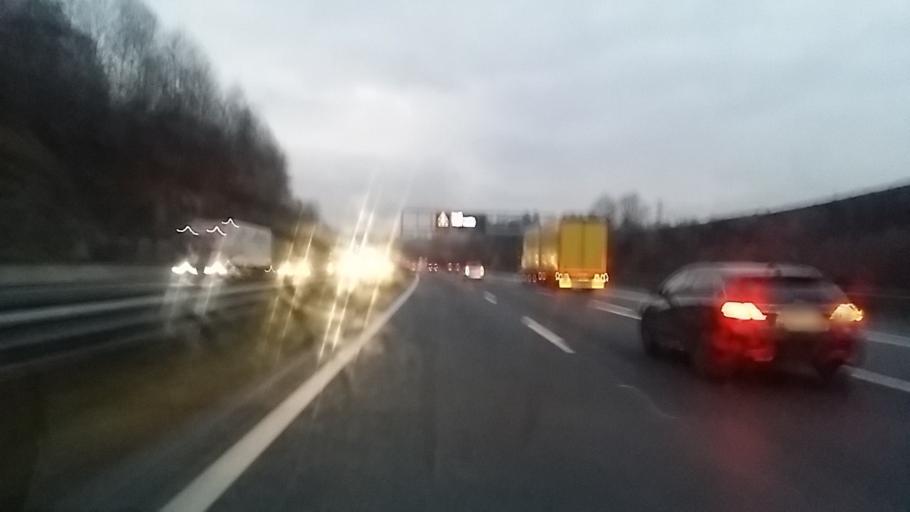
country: CZ
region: Central Bohemia
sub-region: Okres Praha-Vychod
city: Mnichovice
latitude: 49.9311
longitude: 14.6941
